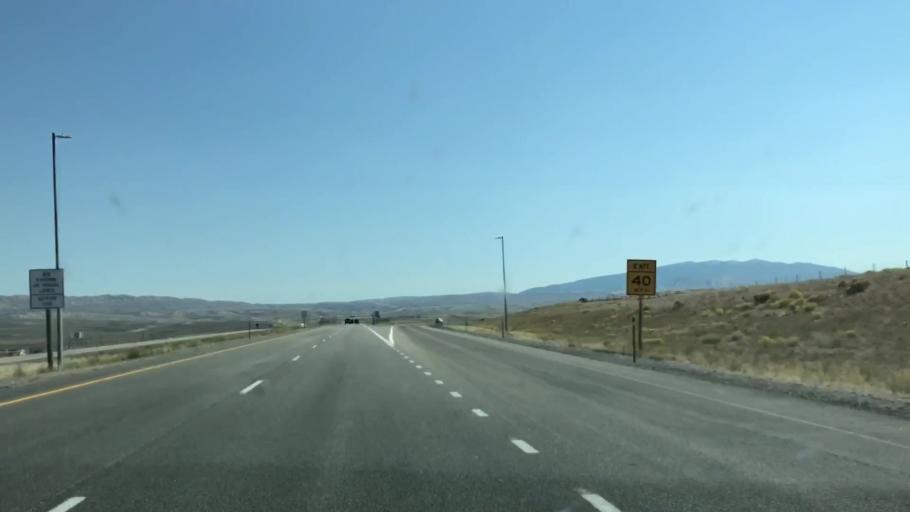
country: US
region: Wyoming
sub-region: Carbon County
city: Saratoga
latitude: 41.7408
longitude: -106.8394
